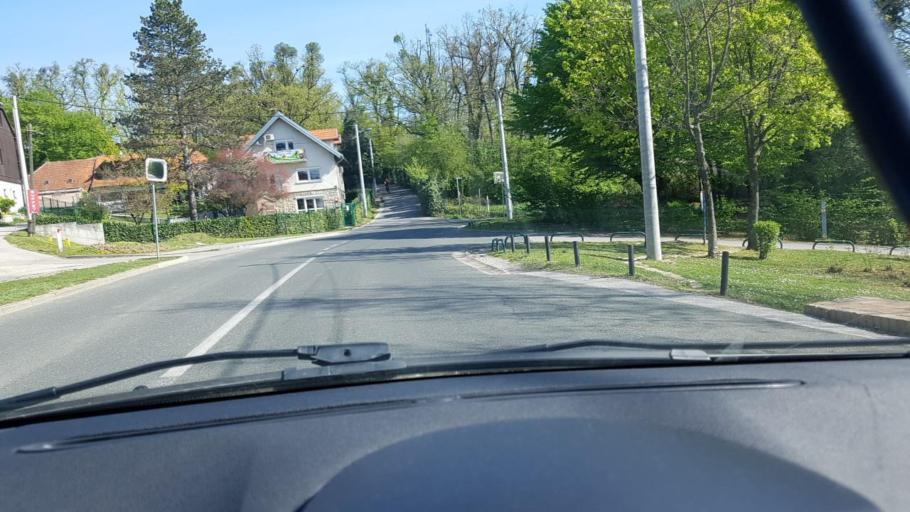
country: HR
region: Grad Zagreb
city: Zagreb
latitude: 45.8457
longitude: 15.9819
